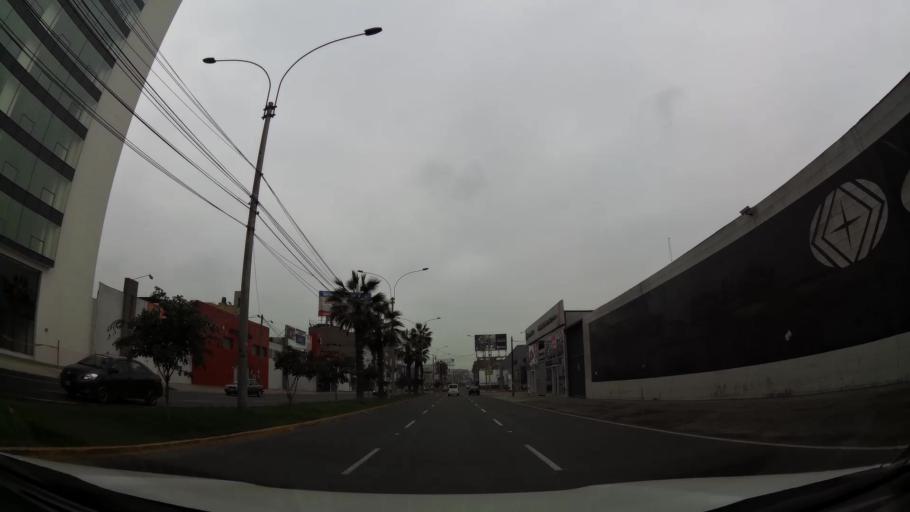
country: PE
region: Lima
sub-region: Lima
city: Surco
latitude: -12.1069
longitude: -77.0167
